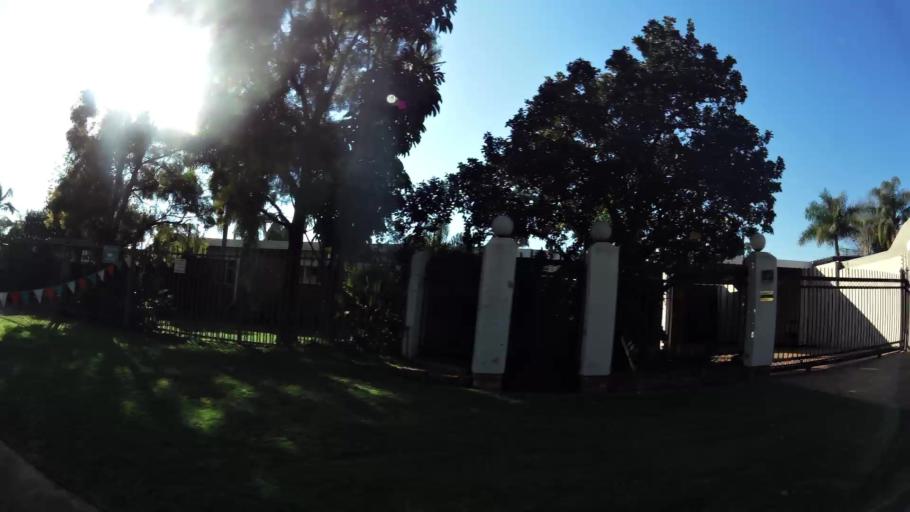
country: ZA
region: Gauteng
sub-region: City of Tshwane Metropolitan Municipality
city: Pretoria
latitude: -25.6771
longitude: 28.2258
